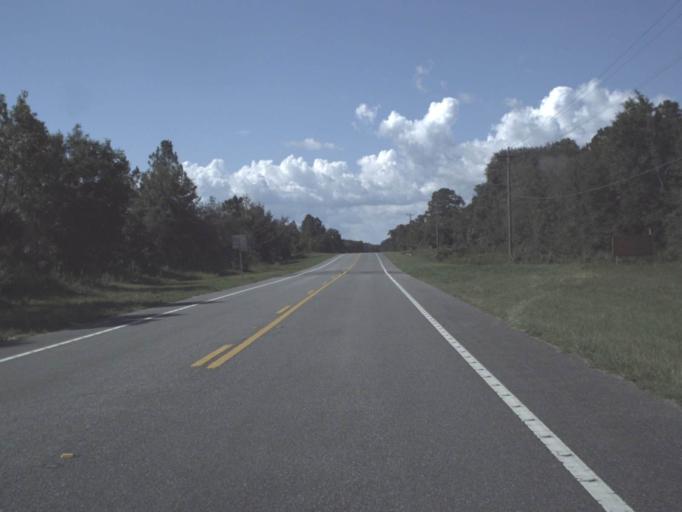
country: US
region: Florida
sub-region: Taylor County
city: Steinhatchee
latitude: 29.6992
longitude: -83.3572
